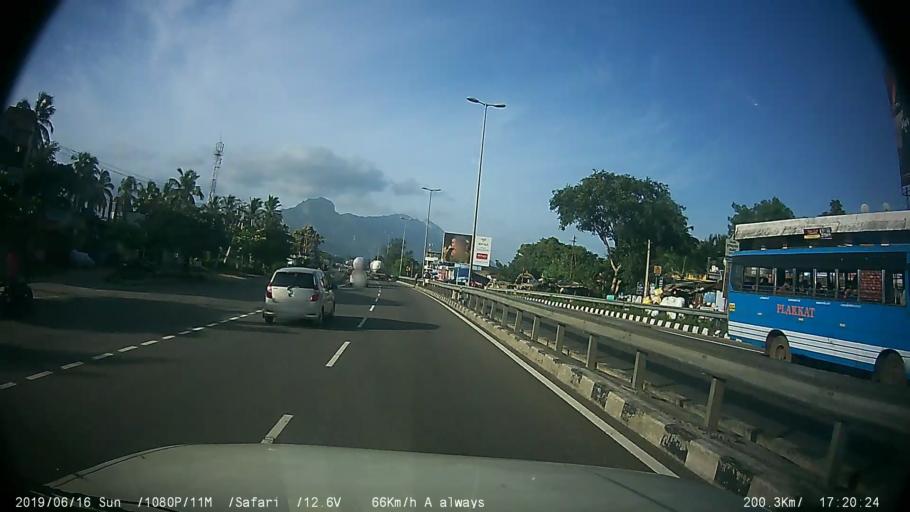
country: IN
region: Kerala
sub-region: Palakkad district
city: Palakkad
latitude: 10.7784
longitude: 76.7118
